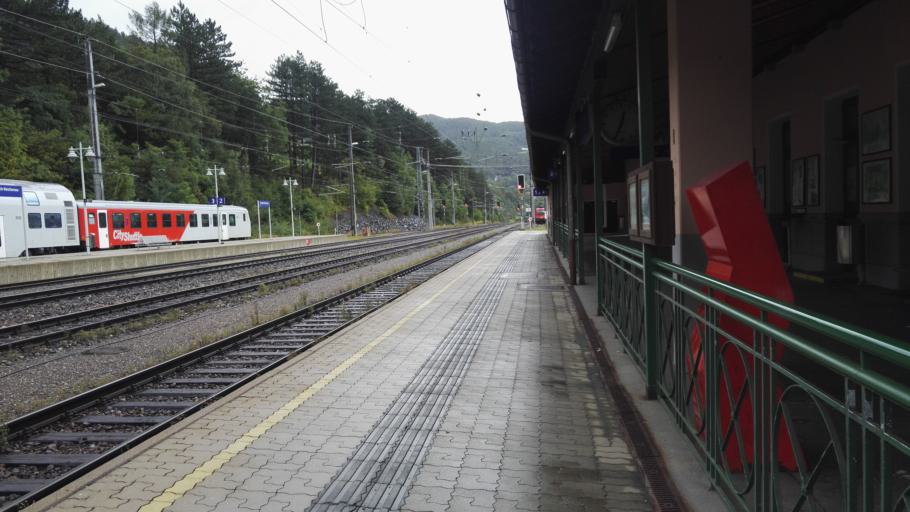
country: AT
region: Lower Austria
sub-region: Politischer Bezirk Neunkirchen
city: Payerbach
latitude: 47.6960
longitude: 15.8630
